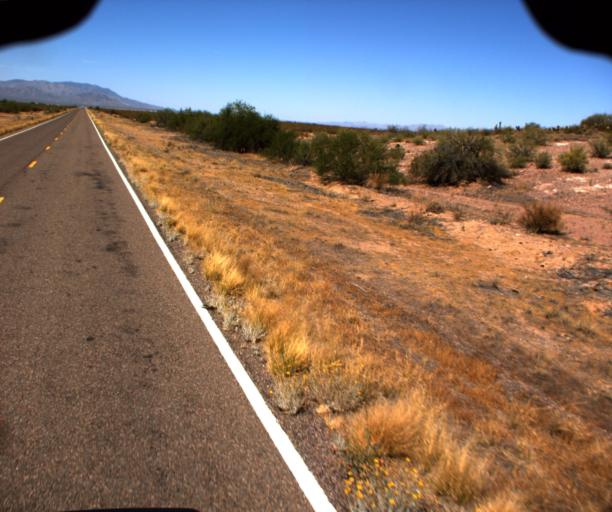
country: US
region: Arizona
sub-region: Yavapai County
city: Congress
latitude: 34.0099
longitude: -113.1094
